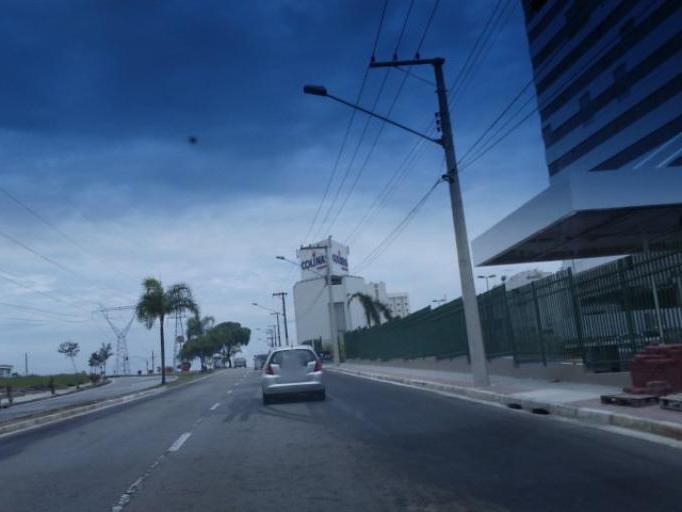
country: BR
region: Sao Paulo
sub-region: Sao Jose Dos Campos
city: Sao Jose dos Campos
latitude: -23.2059
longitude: -45.9081
